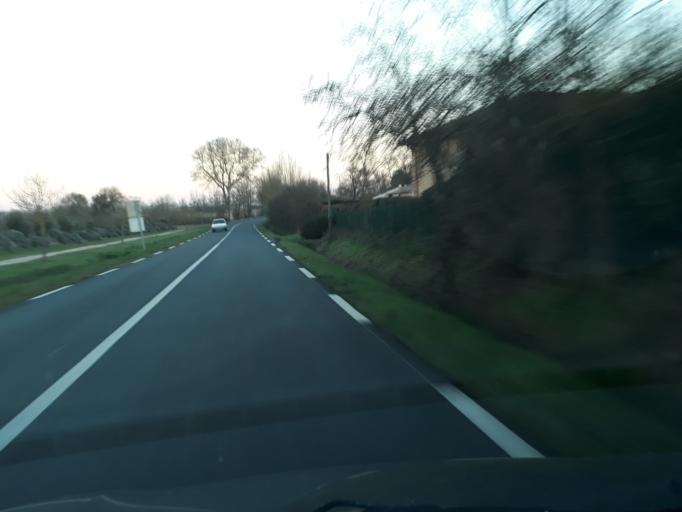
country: FR
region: Midi-Pyrenees
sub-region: Departement de la Haute-Garonne
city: Fontenilles
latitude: 43.5491
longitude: 1.1511
